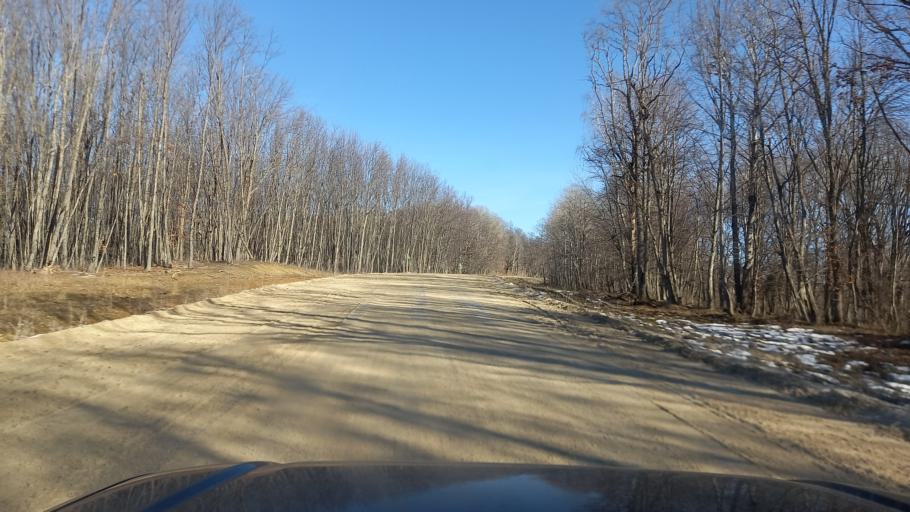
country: RU
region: Adygeya
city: Kamennomostskiy
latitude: 44.2800
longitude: 40.3092
